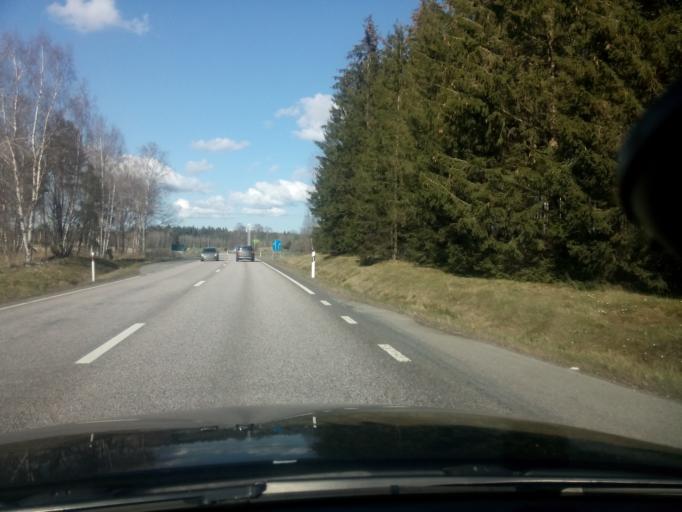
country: SE
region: Soedermanland
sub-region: Strangnas Kommun
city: Akers Styckebruk
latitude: 59.2713
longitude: 16.9688
